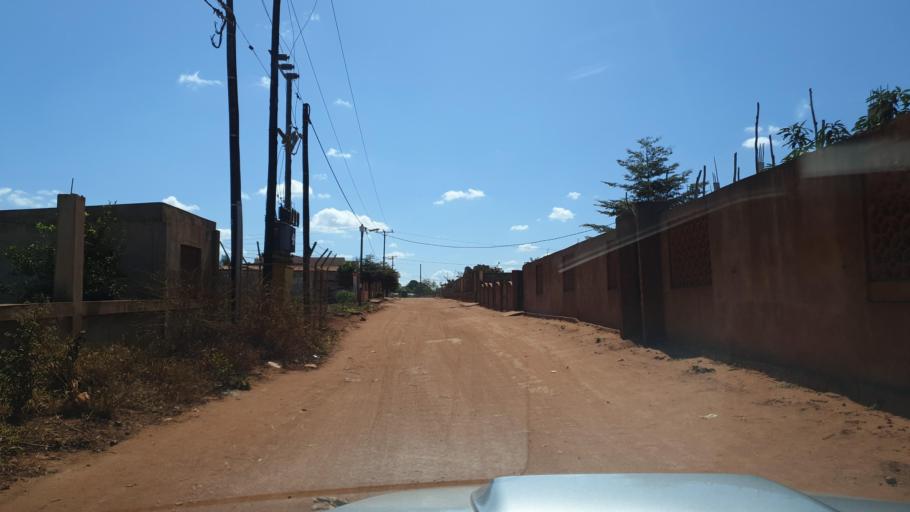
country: MZ
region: Nampula
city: Nampula
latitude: -15.1107
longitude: 39.2061
